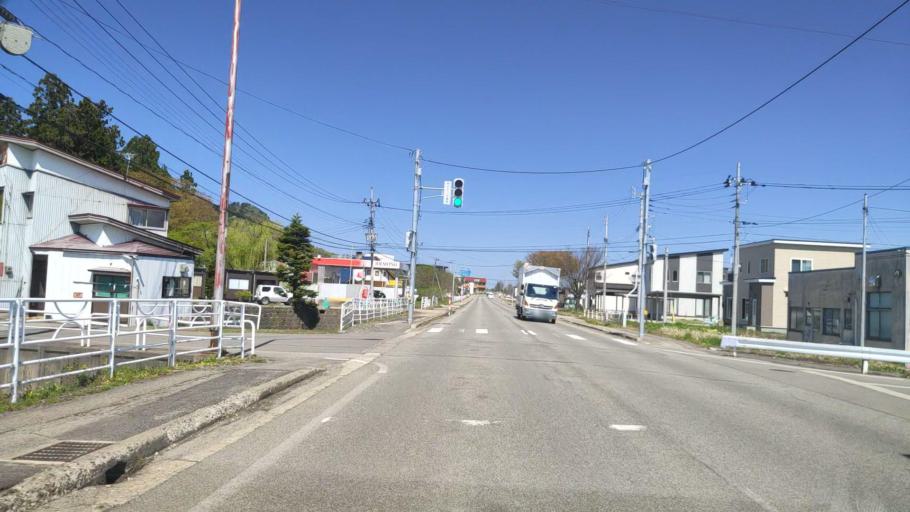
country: JP
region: Akita
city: Omagari
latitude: 39.4728
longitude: 140.4632
